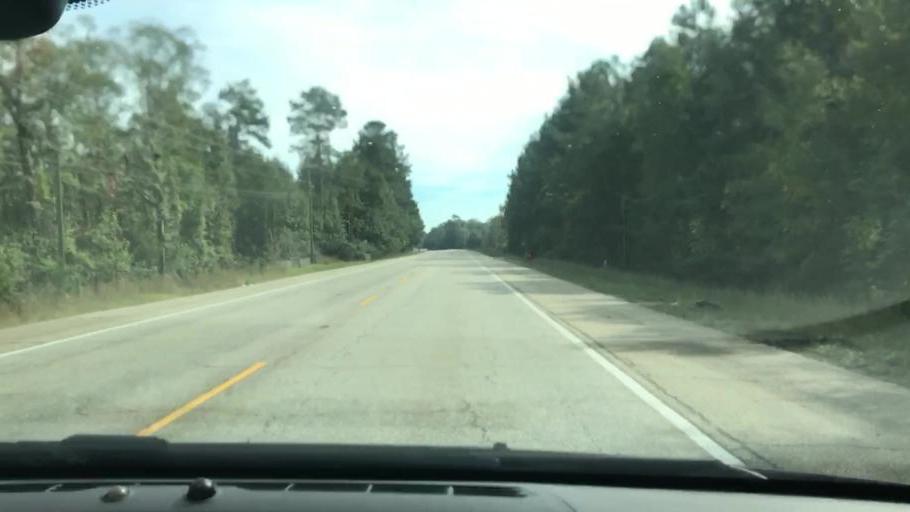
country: US
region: Mississippi
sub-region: Pearl River County
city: Nicholson
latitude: 30.5171
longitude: -89.8339
